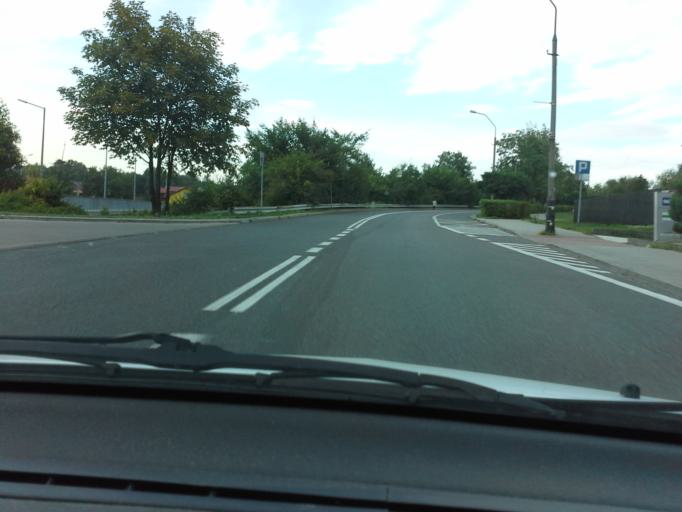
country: PL
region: Lesser Poland Voivodeship
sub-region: Powiat chrzanowski
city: Trzebinia
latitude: 50.1599
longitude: 19.4733
